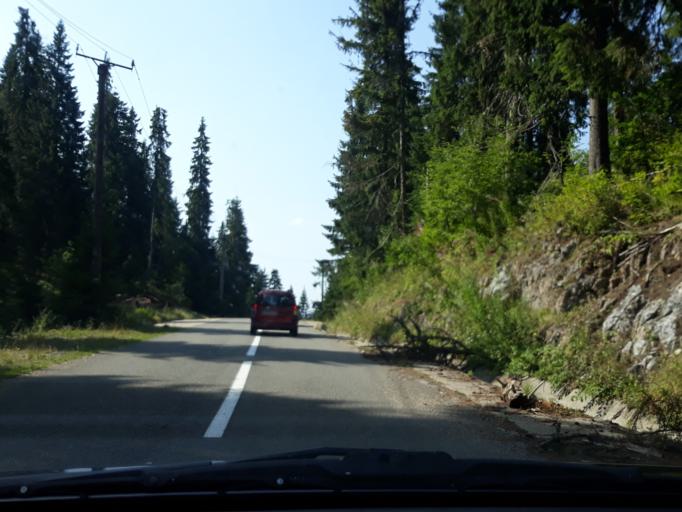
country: RO
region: Alba
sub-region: Comuna Arieseni
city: Arieseni
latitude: 46.5936
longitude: 22.7038
